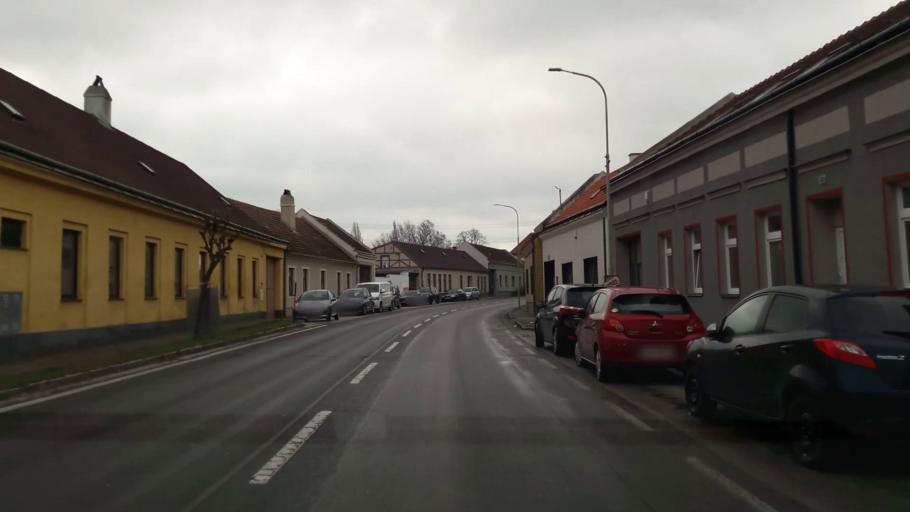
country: AT
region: Lower Austria
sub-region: Politischer Bezirk Wien-Umgebung
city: Lanzendorf
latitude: 48.1064
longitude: 16.4379
